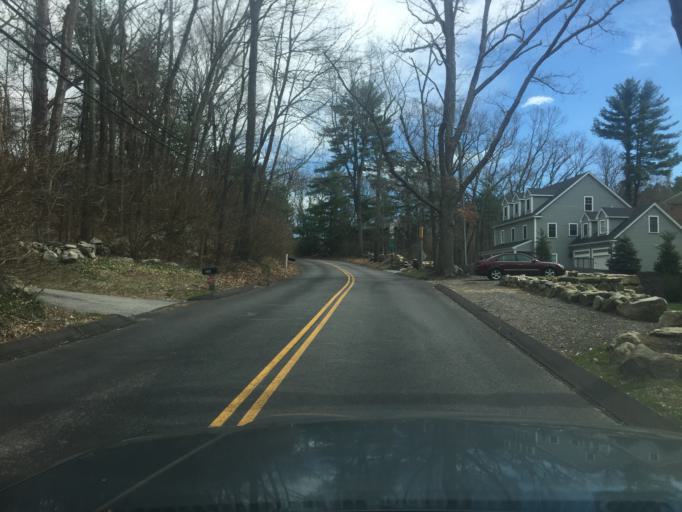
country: US
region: Massachusetts
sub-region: Norfolk County
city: Millis
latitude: 42.1845
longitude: -71.3751
